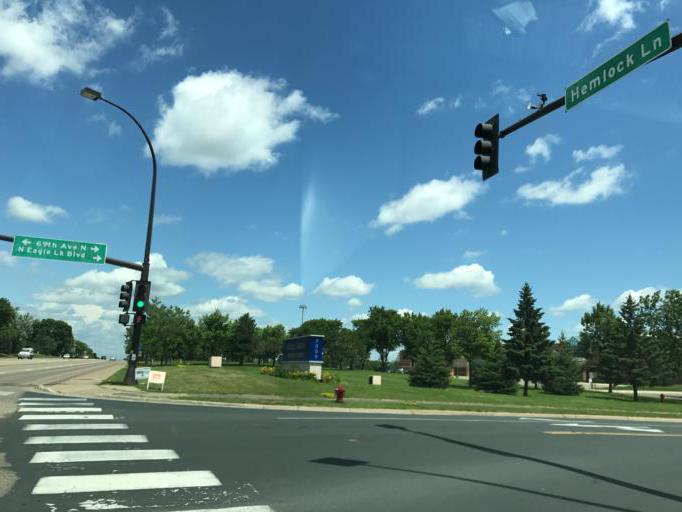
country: US
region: Minnesota
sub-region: Hennepin County
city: Maple Grove
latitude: 45.0800
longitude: -93.4311
